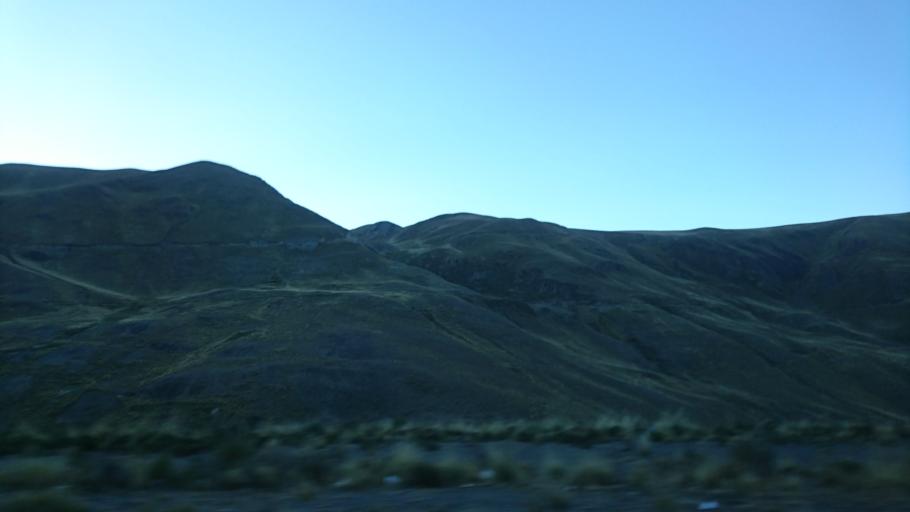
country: BO
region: La Paz
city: La Paz
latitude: -16.4161
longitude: -68.0535
